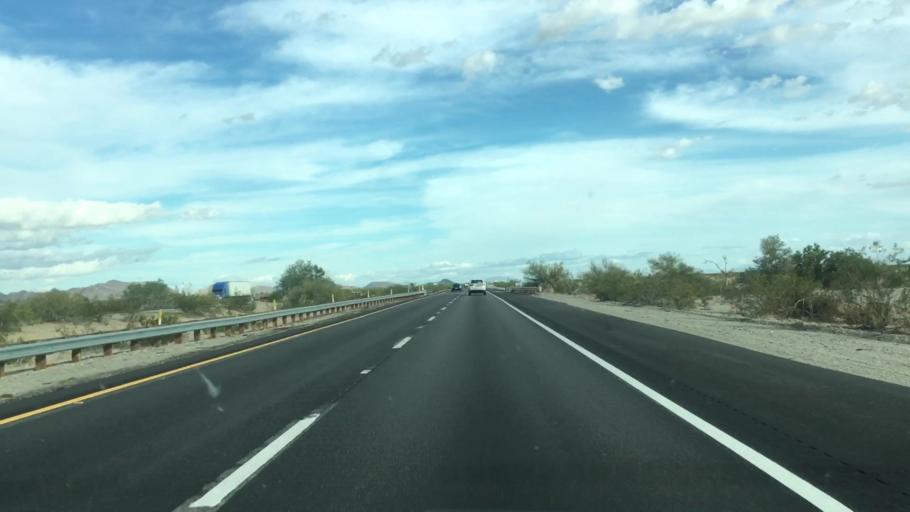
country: US
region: California
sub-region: Riverside County
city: Mesa Verde
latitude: 33.6094
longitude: -114.8467
